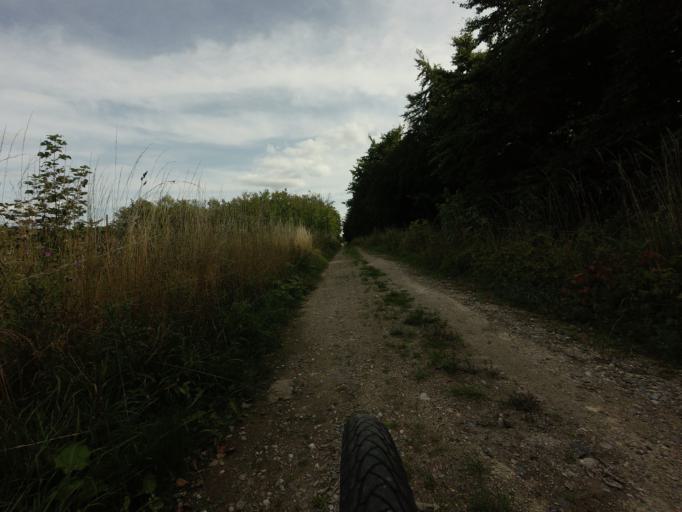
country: DK
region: Zealand
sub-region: Faxe Kommune
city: Fakse Ladeplads
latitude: 55.2300
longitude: 12.1865
